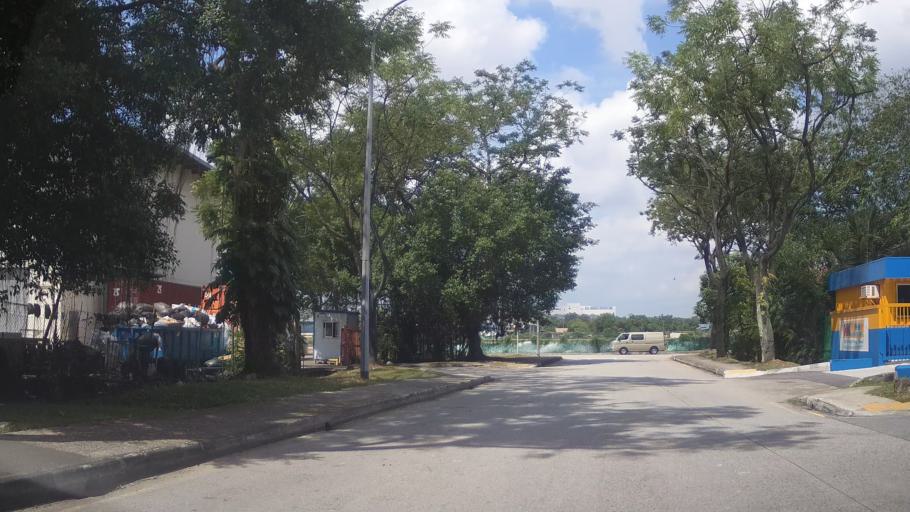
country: SG
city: Singapore
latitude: 1.3288
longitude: 103.7188
